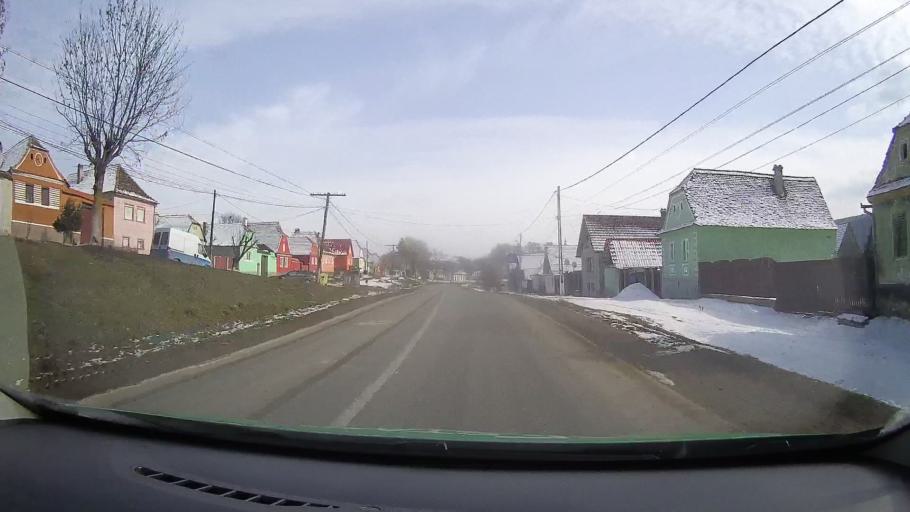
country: RO
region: Mures
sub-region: Comuna Apold
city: Saes
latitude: 46.1596
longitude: 24.7637
